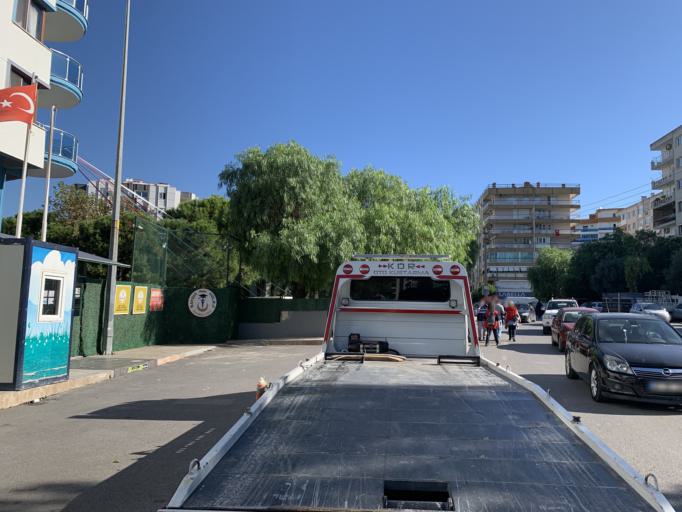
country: TR
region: Izmir
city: Bornova
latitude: 38.4597
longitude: 27.1857
